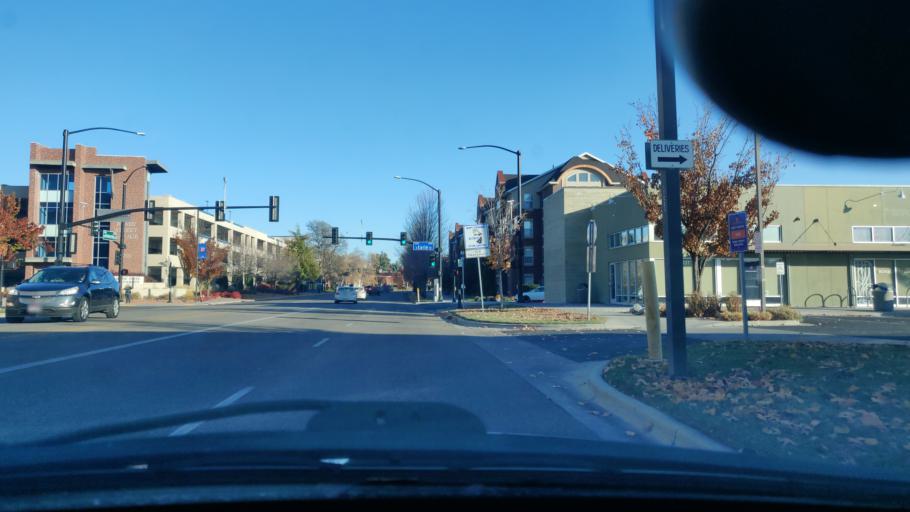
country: US
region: Idaho
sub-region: Ada County
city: Boise
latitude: 43.6051
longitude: -116.2102
